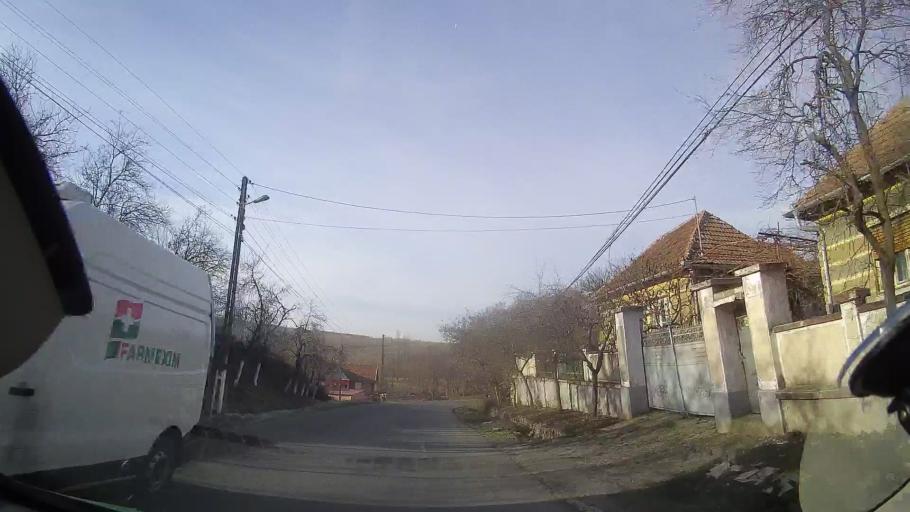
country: RO
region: Bihor
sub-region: Comuna Brusturi
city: Brusturi
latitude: 47.1639
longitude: 22.2252
